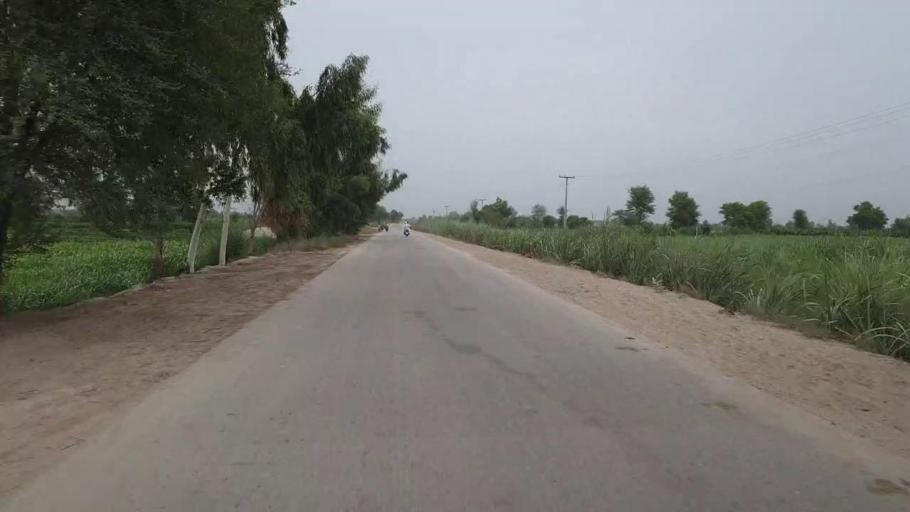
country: PK
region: Sindh
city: Bandhi
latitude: 26.5527
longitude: 68.2119
